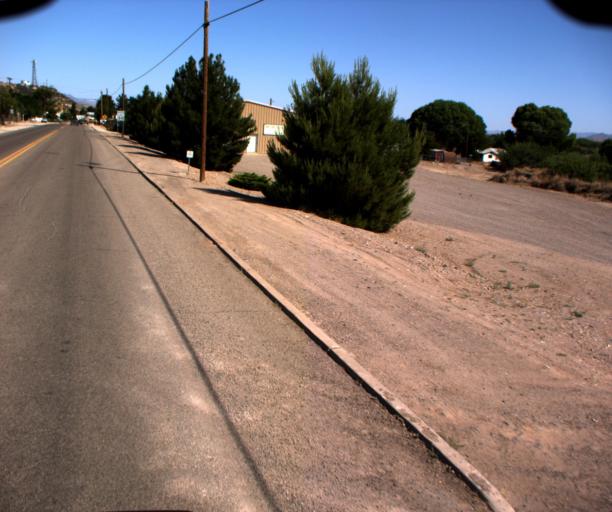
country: US
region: Arizona
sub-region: Greenlee County
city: Clifton
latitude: 32.7125
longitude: -109.0978
